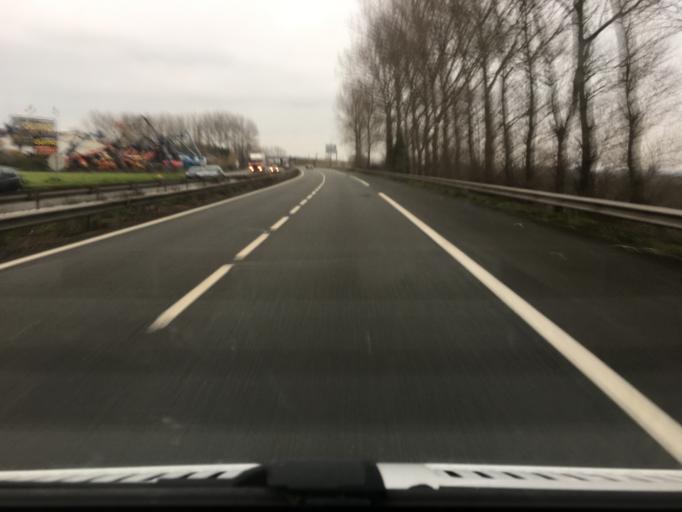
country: FR
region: Nord-Pas-de-Calais
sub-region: Departement du Nord
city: Cappelle-la-Grande
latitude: 50.9963
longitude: 2.3322
